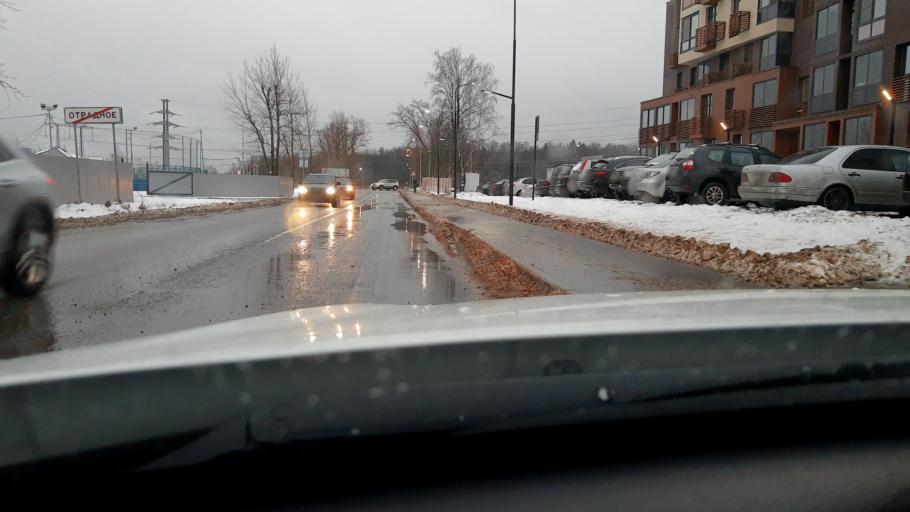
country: RU
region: Moskovskaya
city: Krasnogorsk
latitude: 55.8728
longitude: 37.3107
